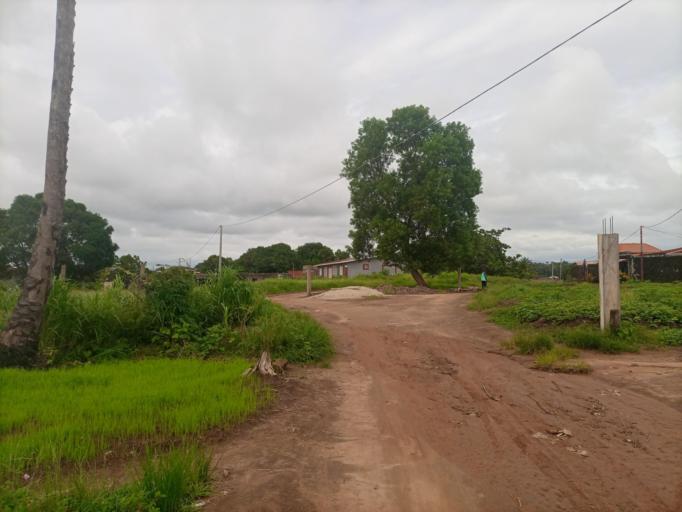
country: SL
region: Northern Province
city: Masoyila
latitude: 8.5968
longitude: -13.1766
